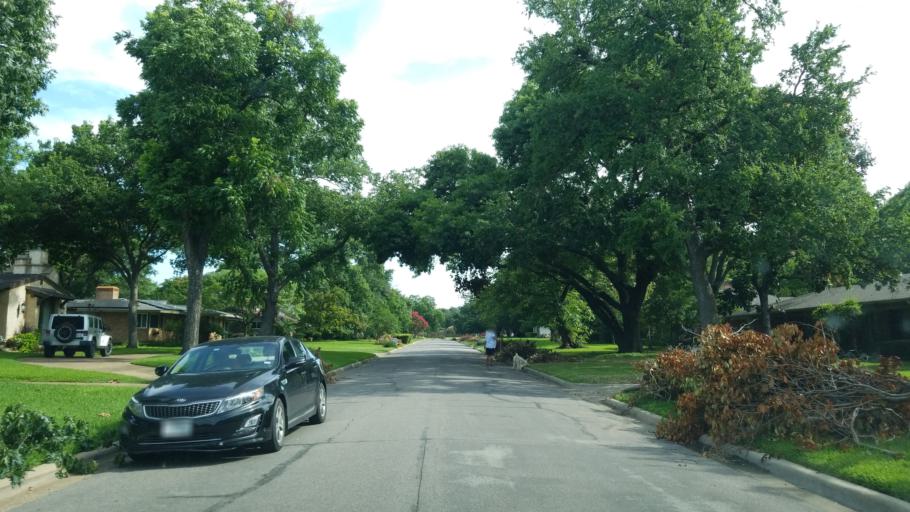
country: US
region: Texas
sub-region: Dallas County
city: Farmers Branch
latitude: 32.8973
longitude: -96.8413
